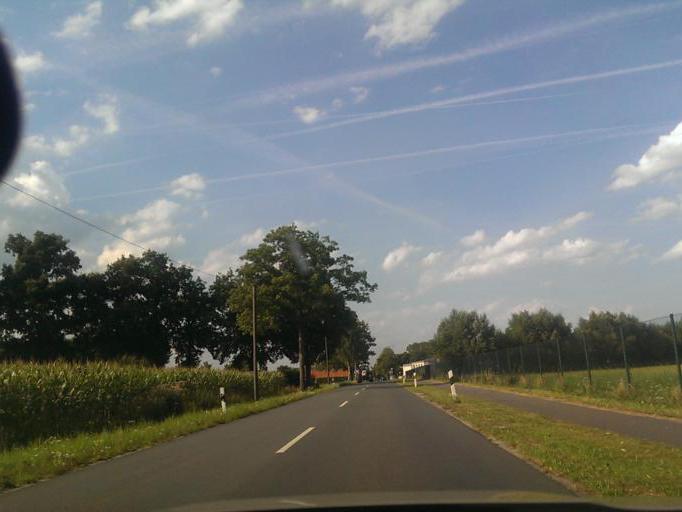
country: DE
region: North Rhine-Westphalia
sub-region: Regierungsbezirk Detmold
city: Delbruck
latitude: 51.7568
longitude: 8.5073
